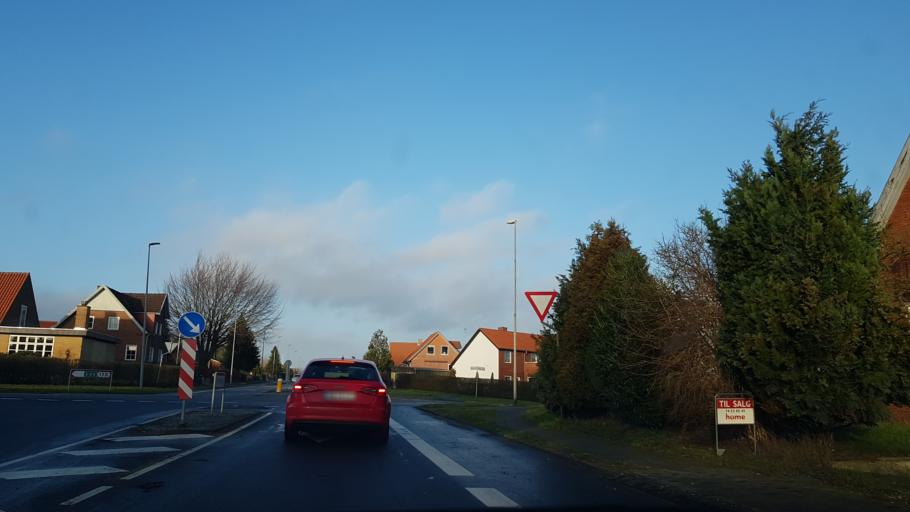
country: DK
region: South Denmark
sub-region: Haderslev Kommune
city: Haderslev
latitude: 55.2420
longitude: 9.4995
